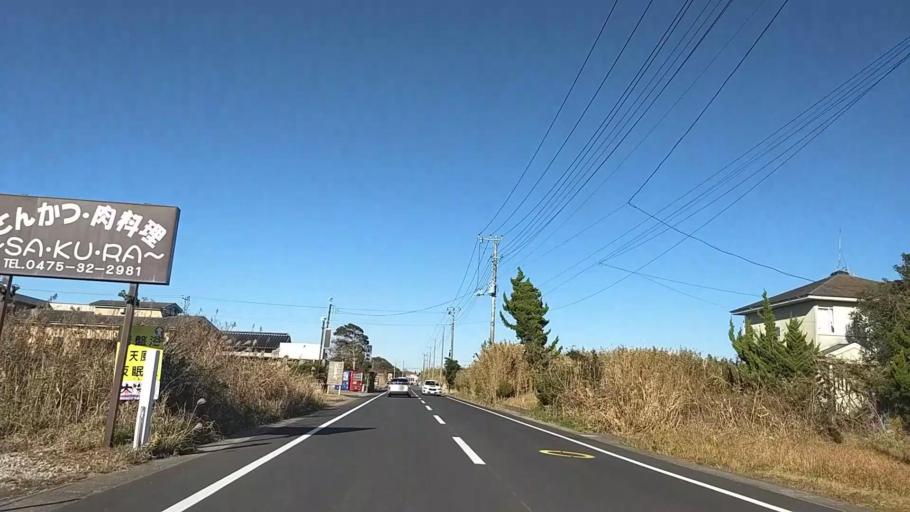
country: JP
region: Chiba
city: Mobara
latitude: 35.4095
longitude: 140.3884
